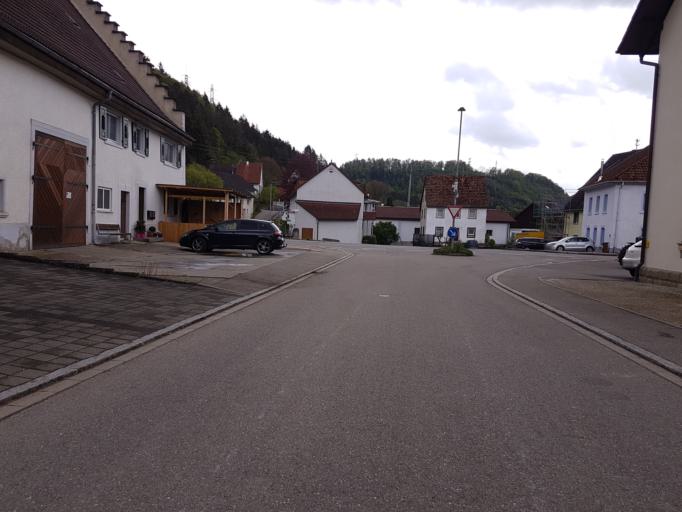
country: CH
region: Schaffhausen
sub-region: Bezirk Schleitheim
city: Schleitheim
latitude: 47.7857
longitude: 8.4970
